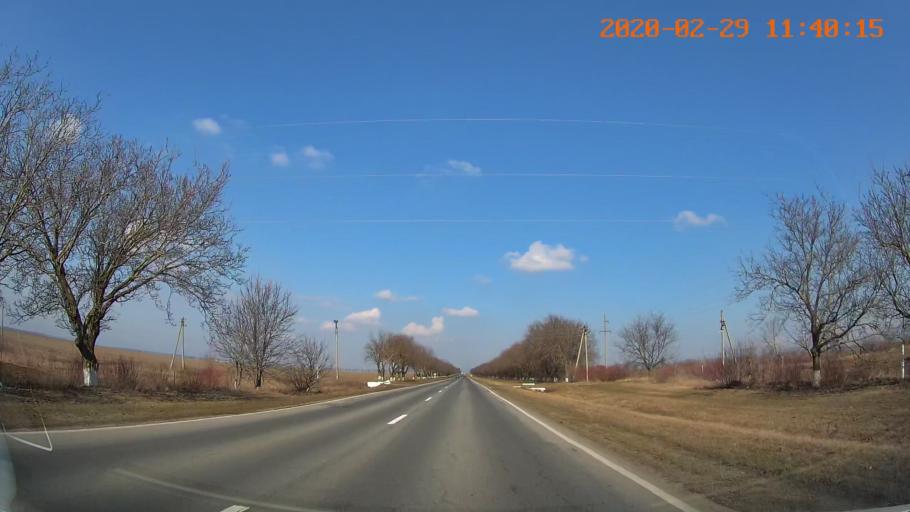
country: MD
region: Rezina
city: Saharna
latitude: 47.6532
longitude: 29.0210
